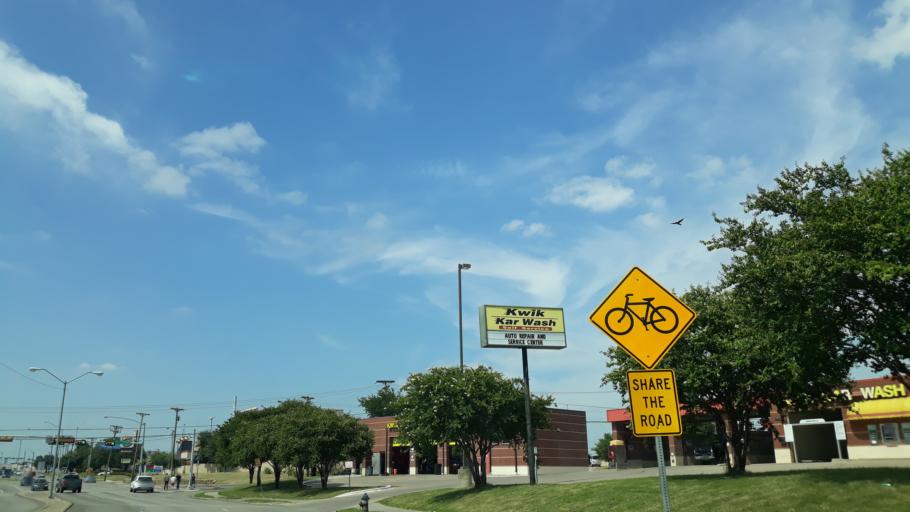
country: US
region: Texas
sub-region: Dallas County
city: Irving
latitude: 32.8322
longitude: -97.0097
